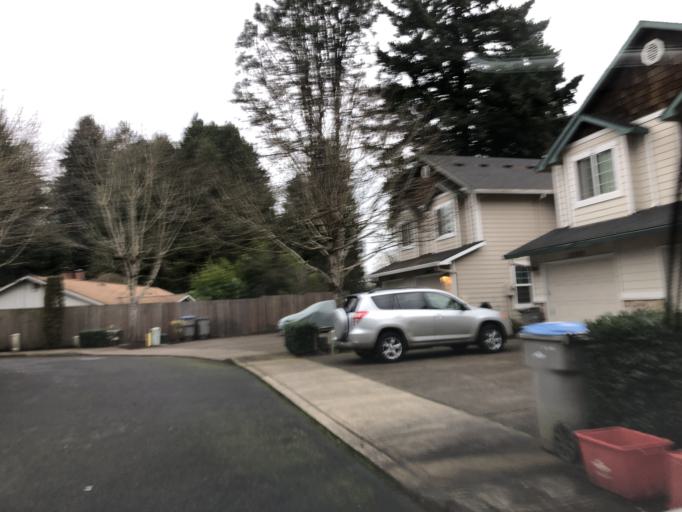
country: US
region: Oregon
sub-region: Washington County
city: Tigard
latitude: 45.4269
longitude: -122.7914
